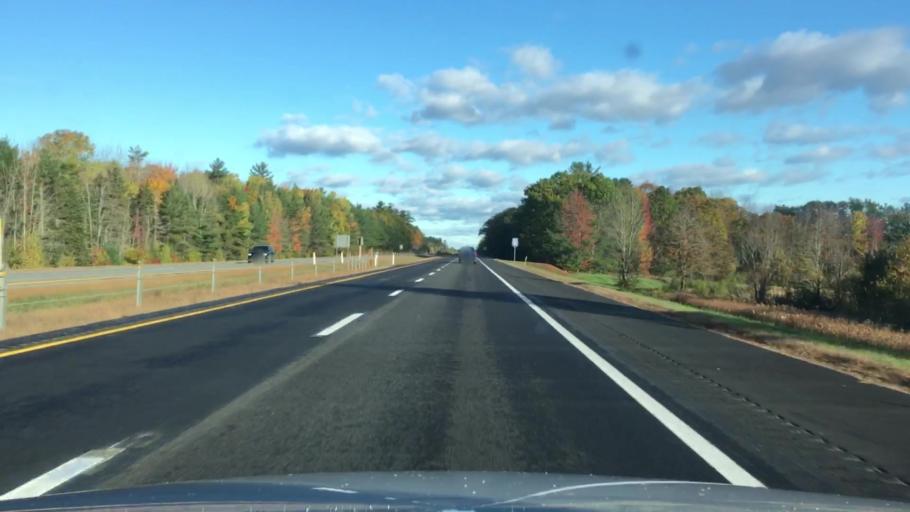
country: US
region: Maine
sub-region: Penobscot County
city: Orono
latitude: 44.9087
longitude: -68.6949
